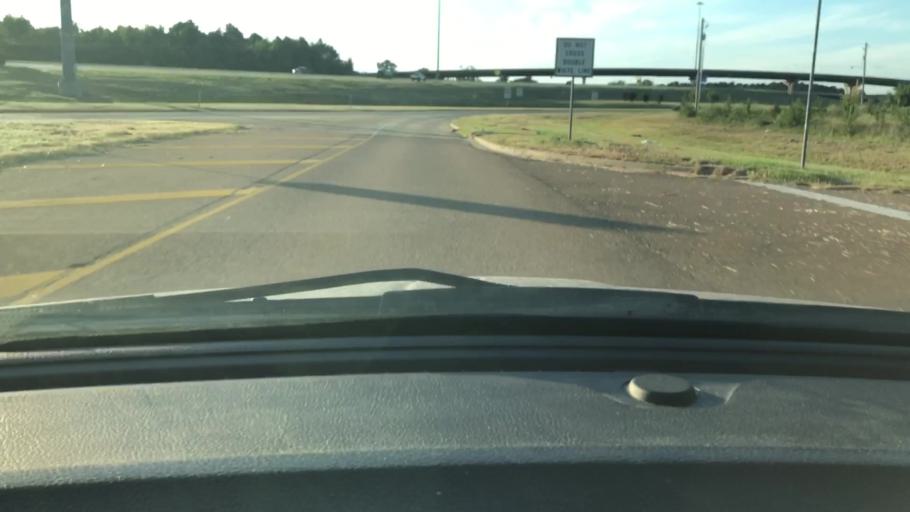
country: US
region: Texas
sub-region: Bowie County
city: Wake Village
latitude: 33.3901
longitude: -94.0962
